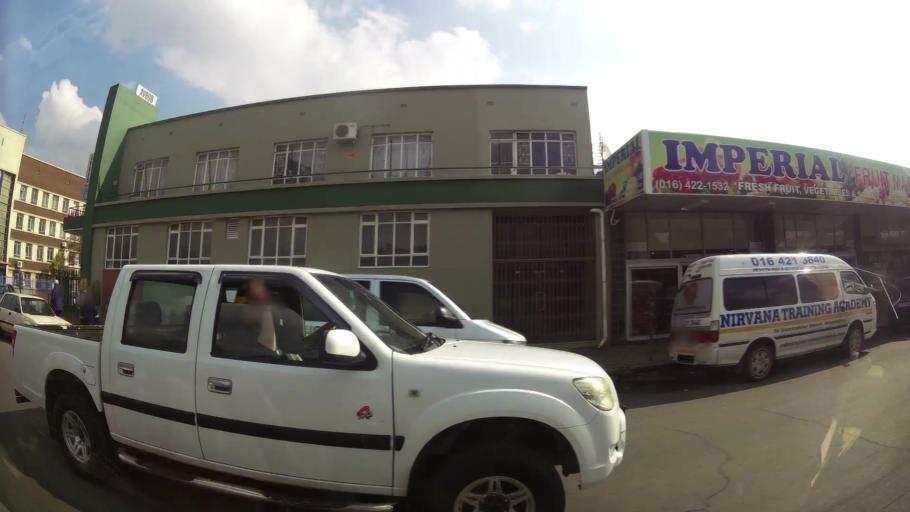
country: ZA
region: Gauteng
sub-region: Sedibeng District Municipality
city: Vereeniging
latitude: -26.6792
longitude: 27.9306
